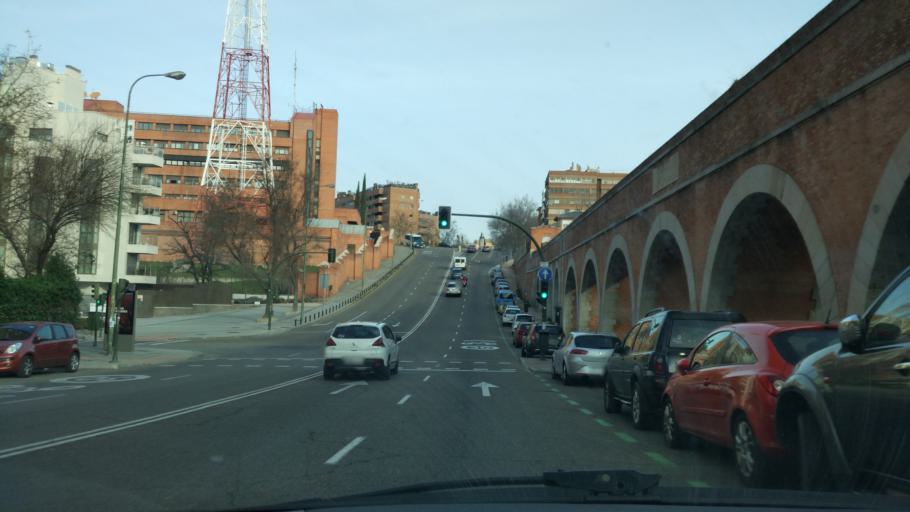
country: ES
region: Madrid
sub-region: Provincia de Madrid
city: Tetuan de las Victorias
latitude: 40.4507
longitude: -3.7107
